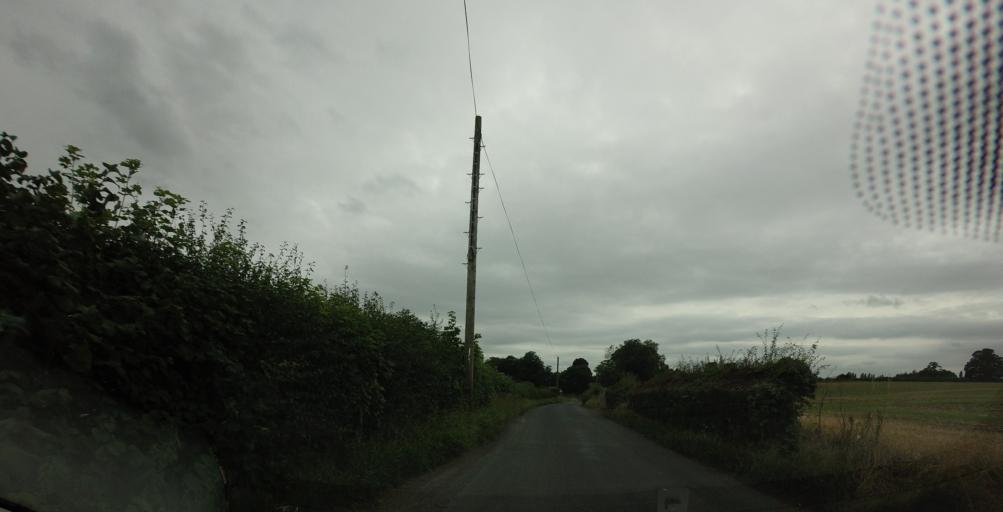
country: GB
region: England
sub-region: North Yorkshire
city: Ripon
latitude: 54.1175
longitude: -1.5173
